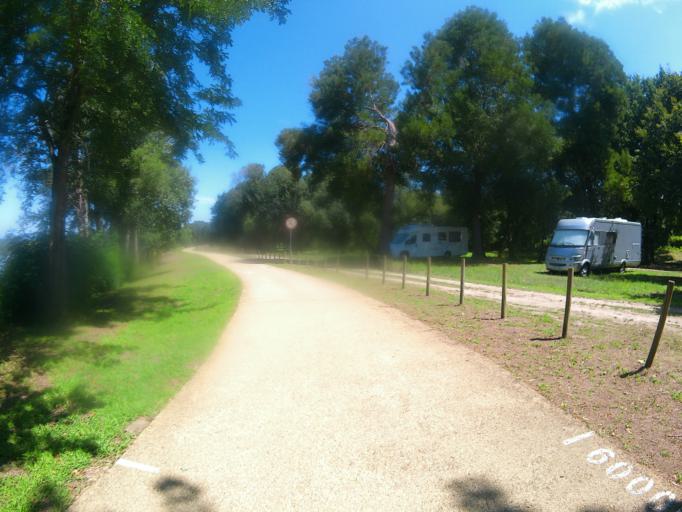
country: PT
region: Viana do Castelo
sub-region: Vila Nova de Cerveira
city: Vila Nova de Cerveira
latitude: 41.9600
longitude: -8.7451
